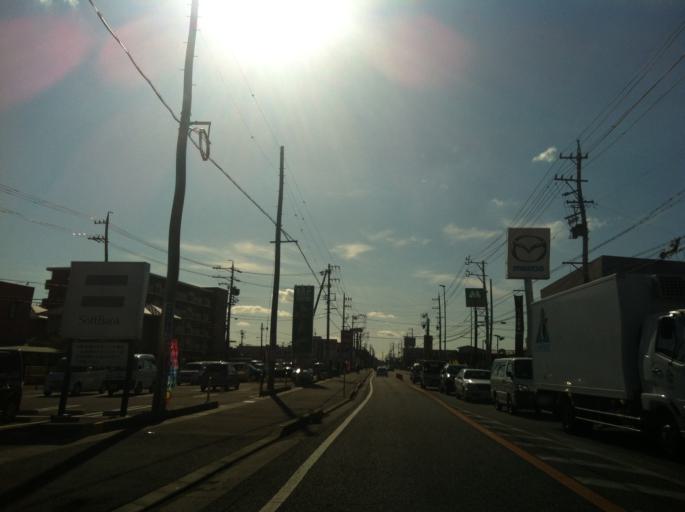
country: JP
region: Shizuoka
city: Fujieda
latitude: 34.8815
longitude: 138.2730
